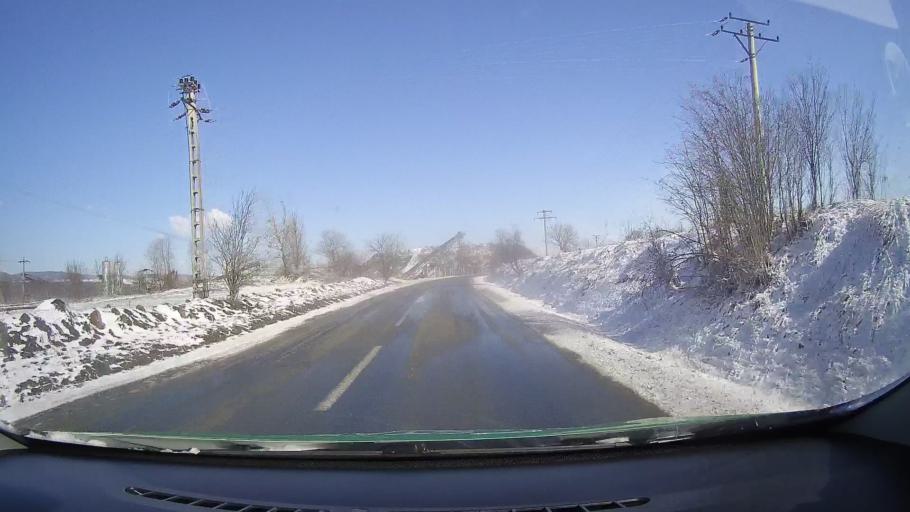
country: RO
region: Sibiu
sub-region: Comuna Racovita
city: Racovita
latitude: 45.6719
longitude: 24.3229
